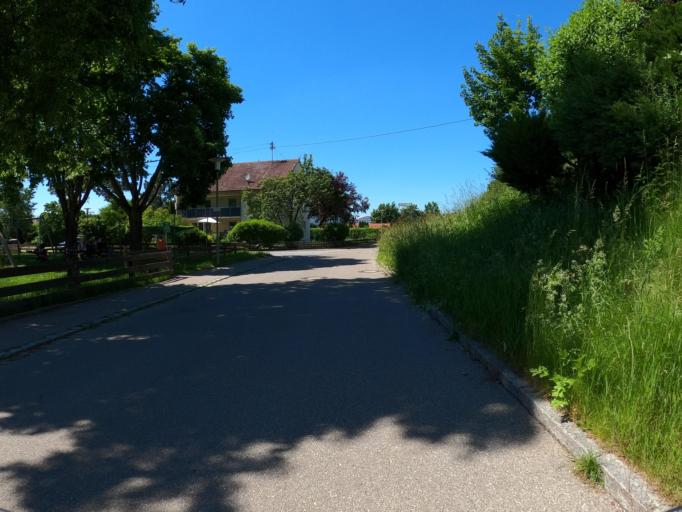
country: DE
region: Bavaria
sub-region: Swabia
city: Pfaffenhofen an der Roth
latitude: 48.3675
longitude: 10.1536
